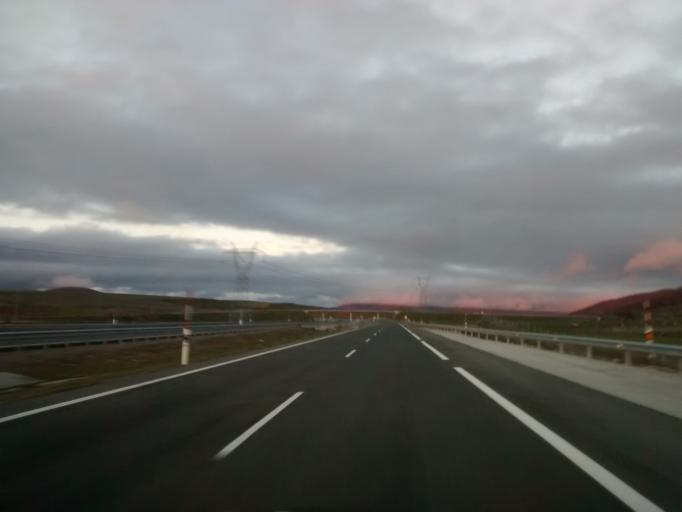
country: ES
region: Cantabria
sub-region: Provincia de Cantabria
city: Mataporquera
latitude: 42.8470
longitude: -4.1720
